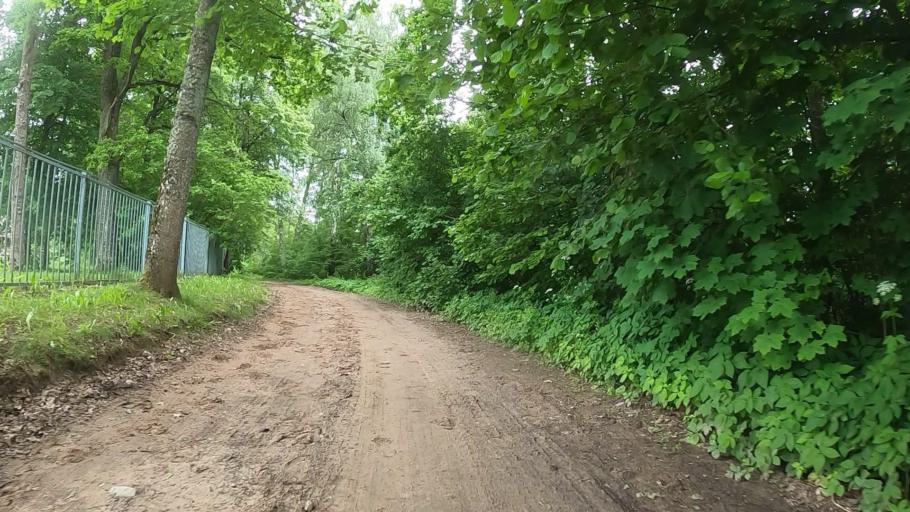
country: LV
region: Ozolnieku
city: Ozolnieki
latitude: 56.7023
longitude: 23.7892
